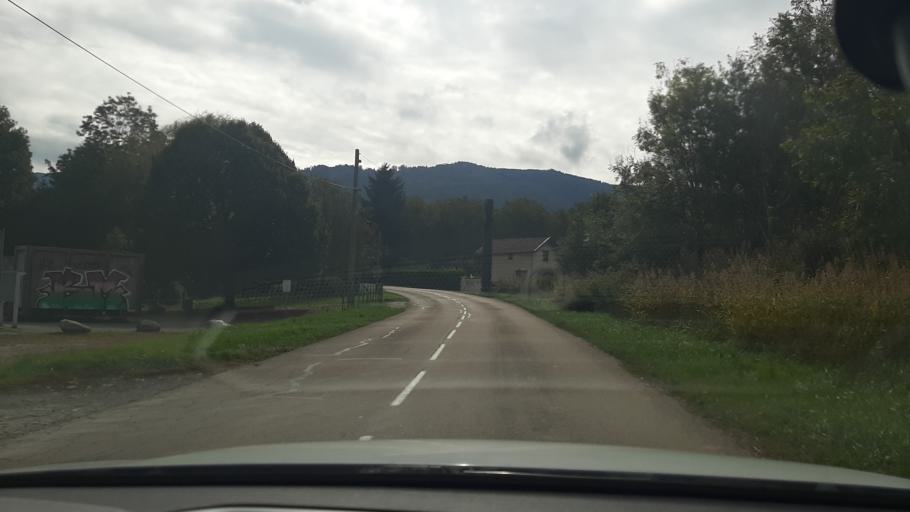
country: FR
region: Rhone-Alpes
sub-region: Departement de la Savoie
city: Montmelian
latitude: 45.4515
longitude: 6.0625
